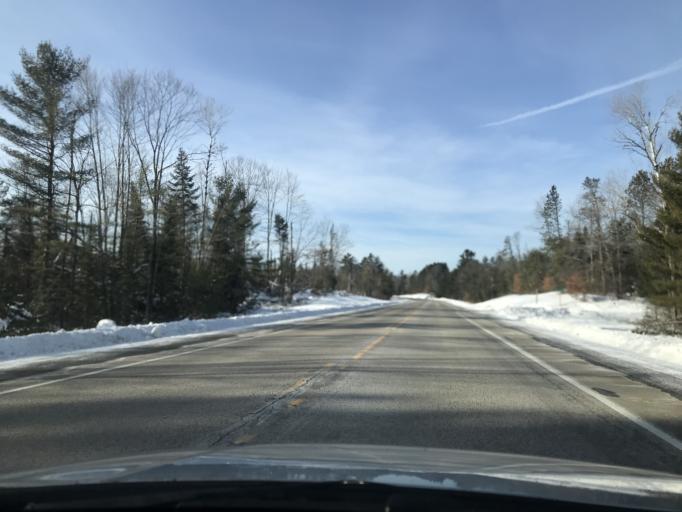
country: US
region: Wisconsin
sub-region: Oconto County
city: Gillett
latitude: 45.1262
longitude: -88.4018
